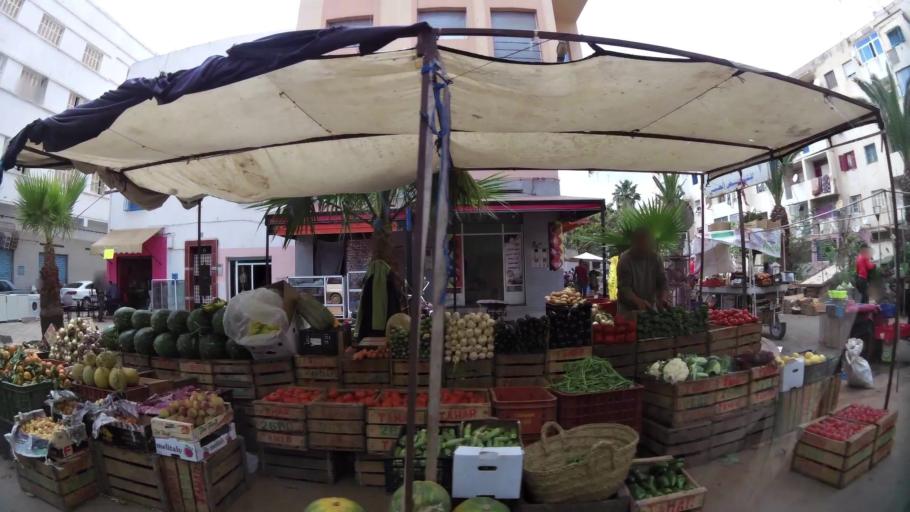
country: MA
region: Oriental
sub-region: Nador
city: Nador
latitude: 35.1746
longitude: -2.9286
